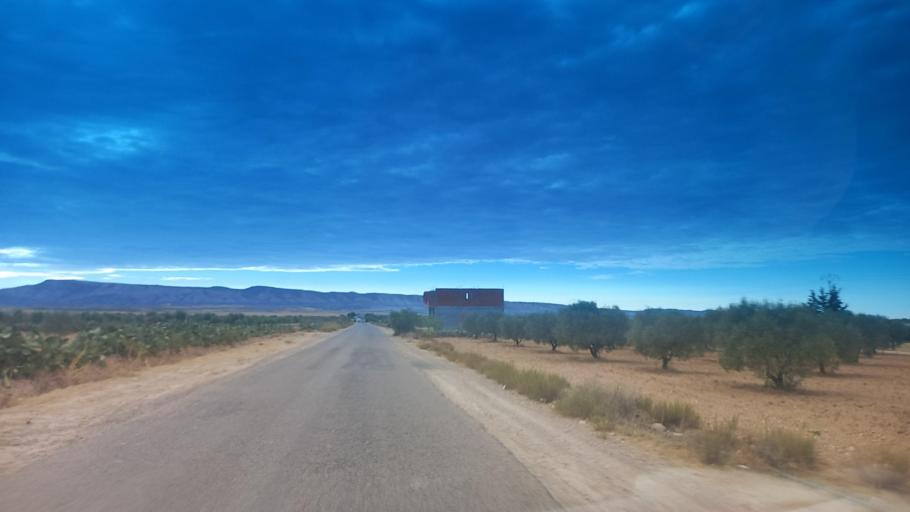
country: TN
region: Al Qasrayn
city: Sbiba
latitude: 35.3695
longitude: 9.0772
